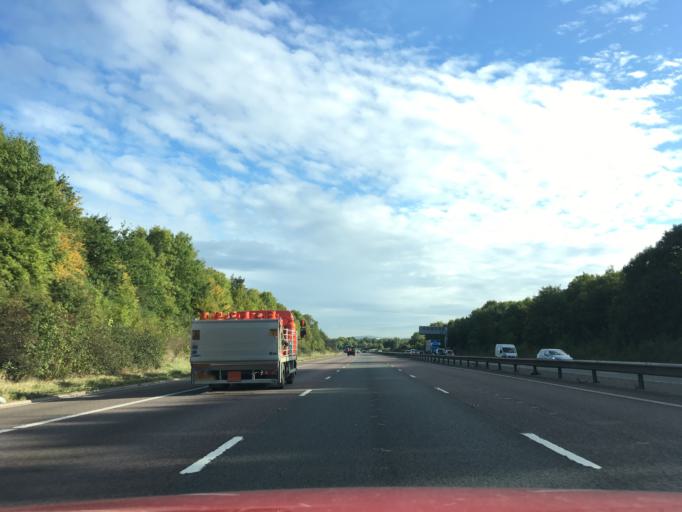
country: GB
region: England
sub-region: Gloucestershire
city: Churchdown
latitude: 51.8705
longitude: -2.1571
